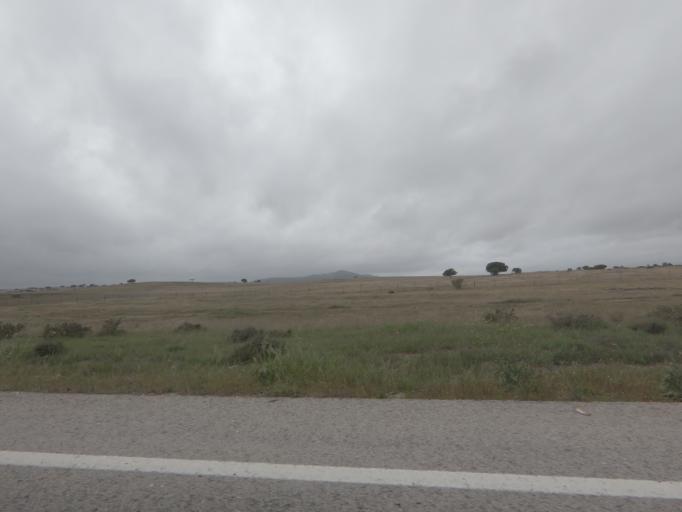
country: ES
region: Extremadura
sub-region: Provincia de Caceres
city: Malpartida de Caceres
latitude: 39.3254
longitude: -6.4957
